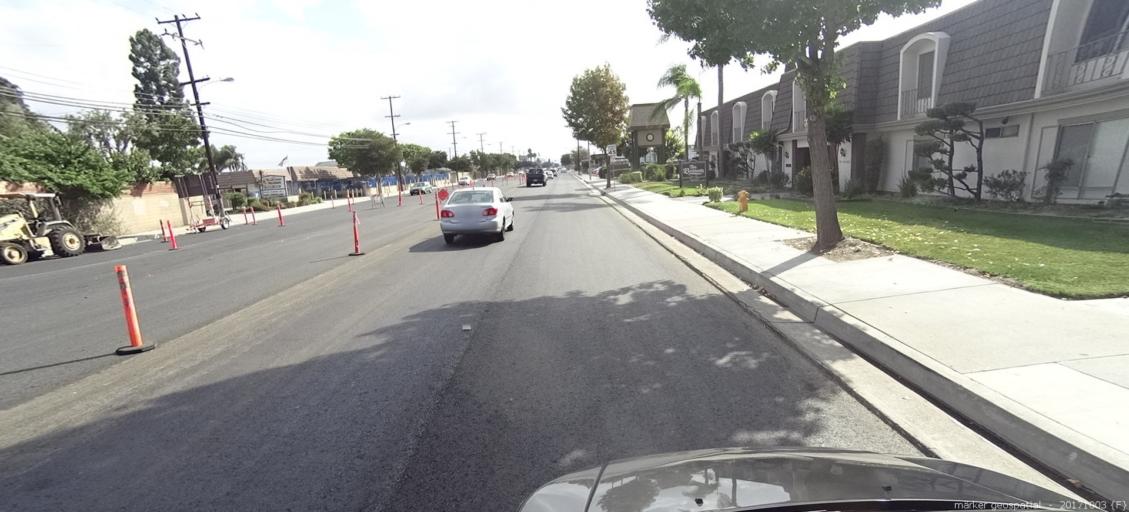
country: US
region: California
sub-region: Orange County
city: Garden Grove
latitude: 33.7595
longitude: -117.9466
